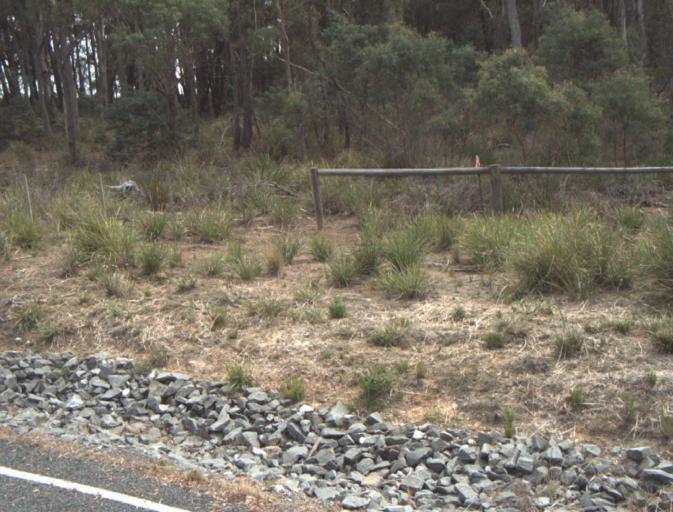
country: AU
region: Tasmania
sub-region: Launceston
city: Mayfield
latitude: -41.2758
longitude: 147.0367
